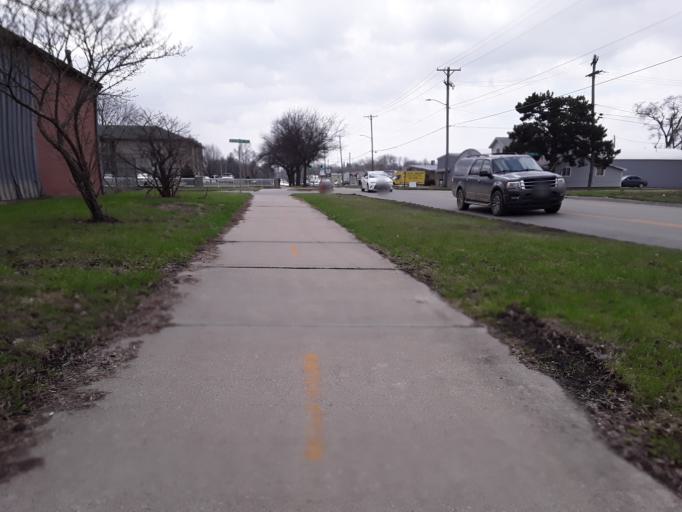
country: US
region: Nebraska
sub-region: Lancaster County
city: Lincoln
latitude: 40.8387
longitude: -96.6727
